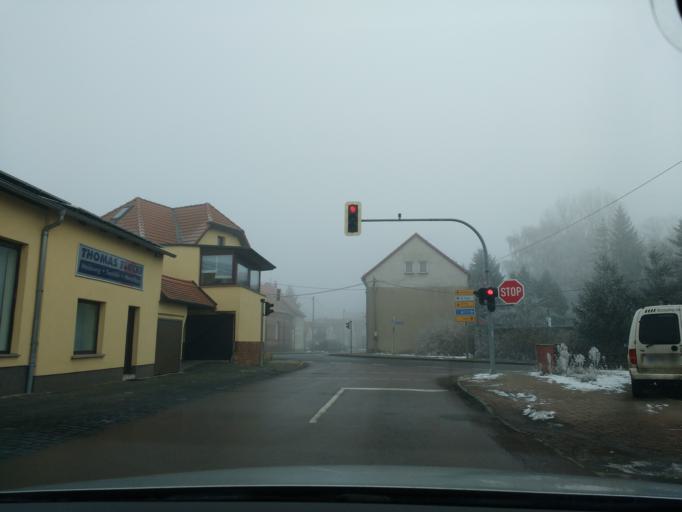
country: DE
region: Saxony-Anhalt
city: Oppin
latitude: 51.5527
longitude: 12.0267
